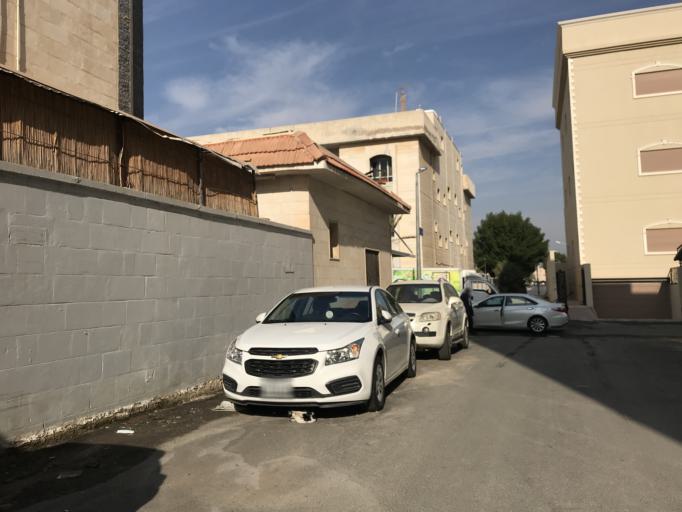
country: KW
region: Muhafazat Hawalli
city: Ar Rumaythiyah
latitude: 29.3049
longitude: 48.0740
